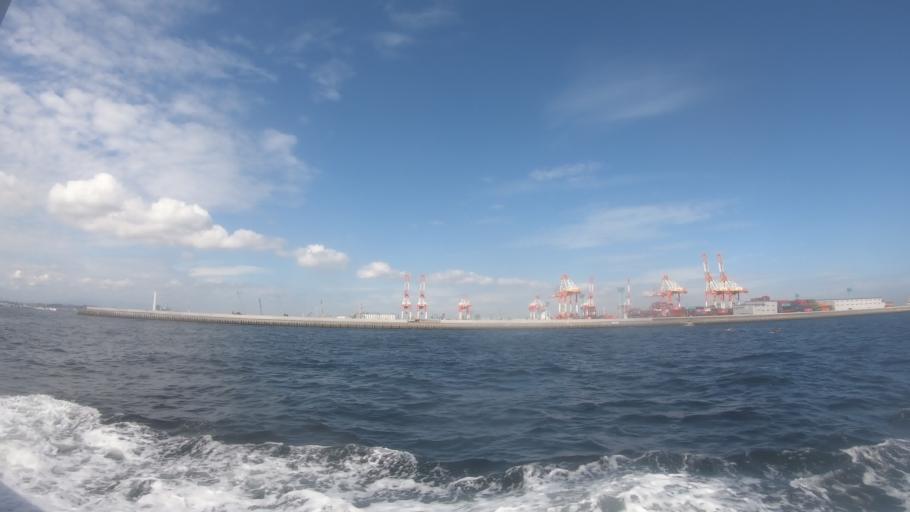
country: JP
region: Kanagawa
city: Yokohama
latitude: 35.3928
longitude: 139.6863
